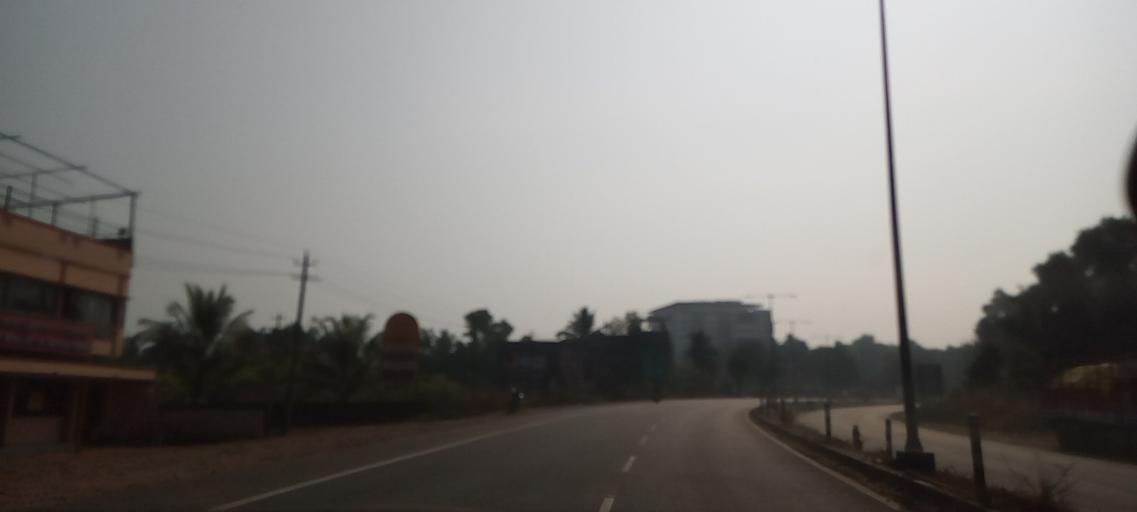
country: IN
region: Karnataka
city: Gangolli
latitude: 13.6784
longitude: 74.6966
